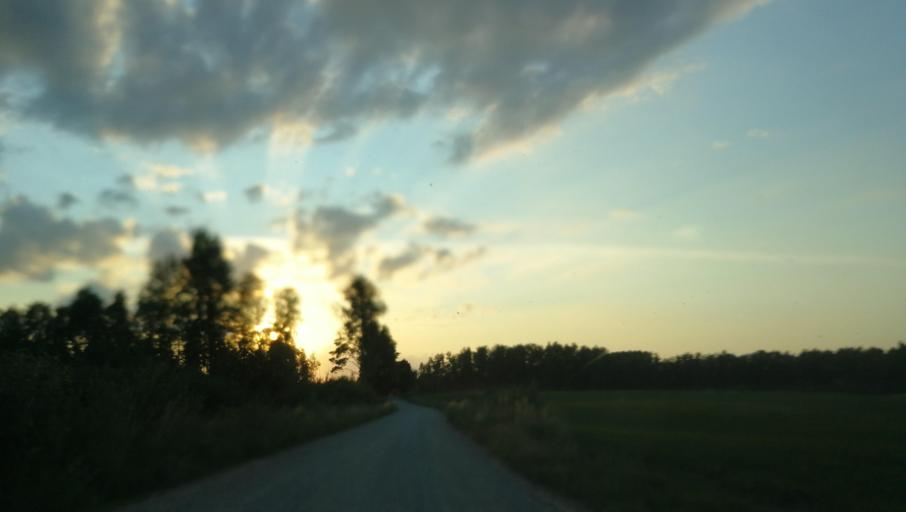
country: LV
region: Amatas Novads
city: Drabesi
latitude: 57.2526
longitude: 25.1727
